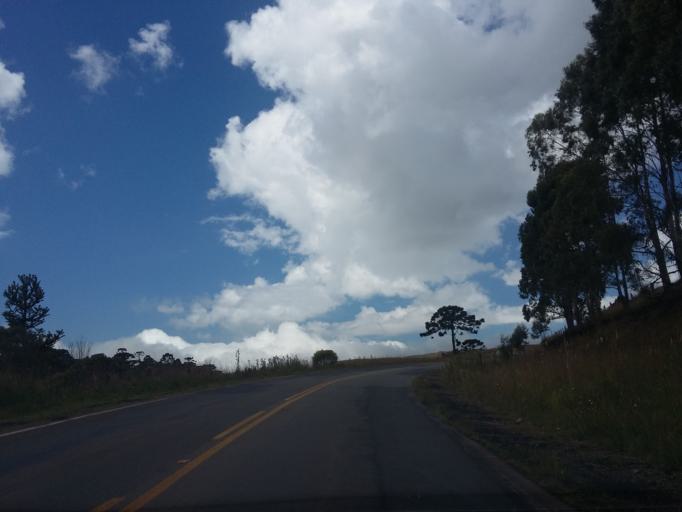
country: BR
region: Santa Catarina
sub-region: Lauro Muller
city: Lauro Muller
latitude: -28.3542
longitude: -49.5919
